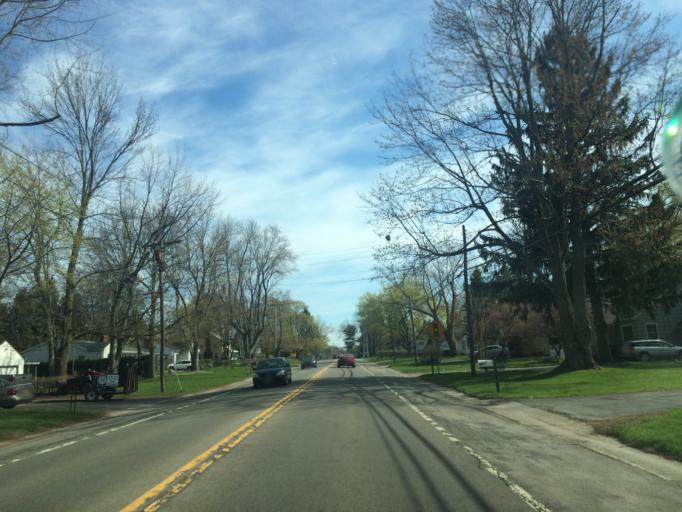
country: US
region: New York
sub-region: Monroe County
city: Webster
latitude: 43.2018
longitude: -77.4303
